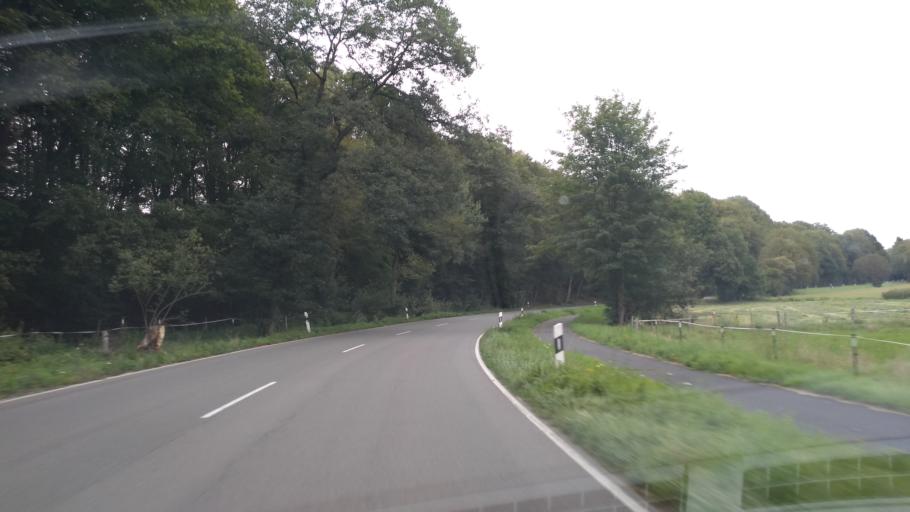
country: DE
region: North Rhine-Westphalia
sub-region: Regierungsbezirk Koln
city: Ruppichteroth
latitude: 50.8862
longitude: 7.4636
